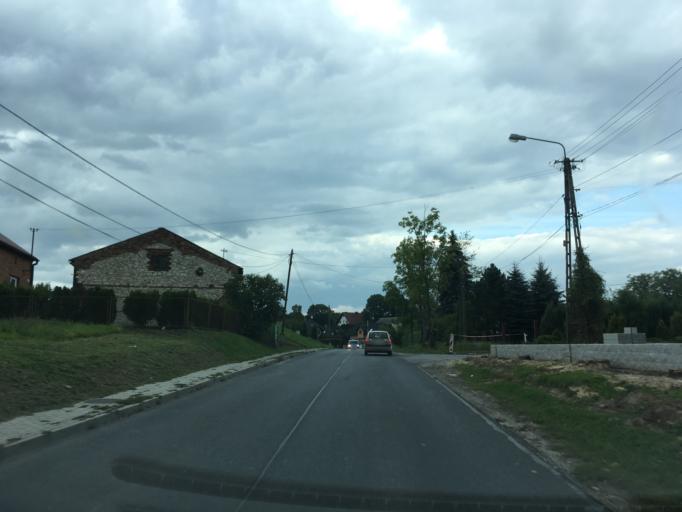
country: PL
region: Lesser Poland Voivodeship
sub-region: Powiat olkuski
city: Wolbrom
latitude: 50.3907
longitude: 19.7621
